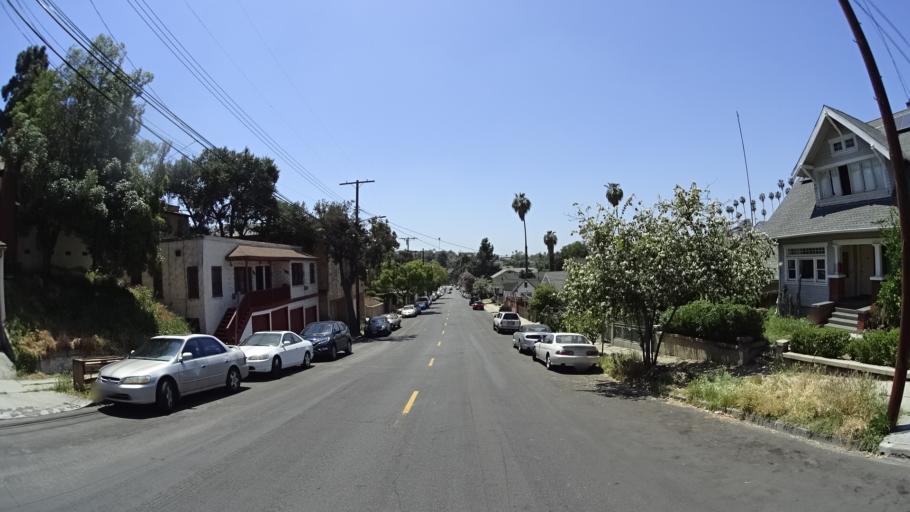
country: US
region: California
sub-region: Los Angeles County
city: Echo Park
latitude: 34.0781
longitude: -118.2528
